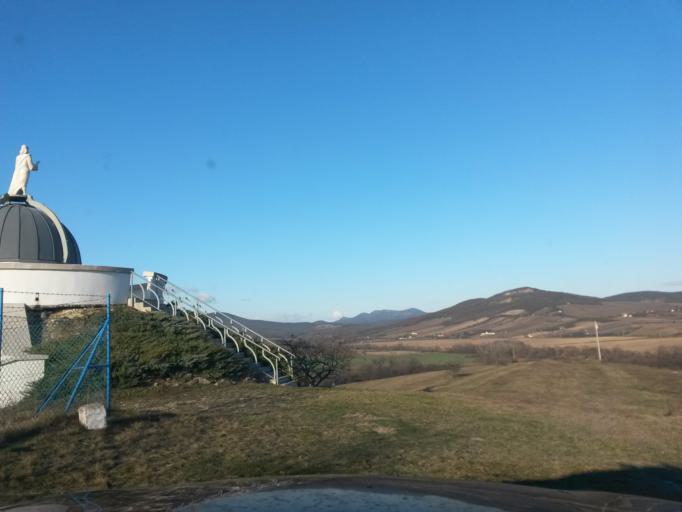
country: HU
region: Borsod-Abauj-Zemplen
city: Sarospatak
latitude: 48.3288
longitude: 21.5384
